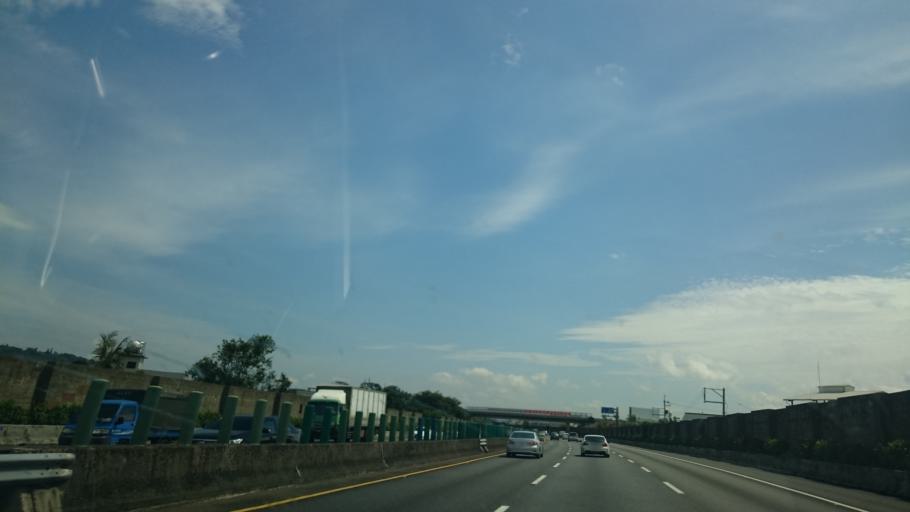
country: TW
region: Taiwan
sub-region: Miaoli
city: Miaoli
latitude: 24.5099
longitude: 120.8077
